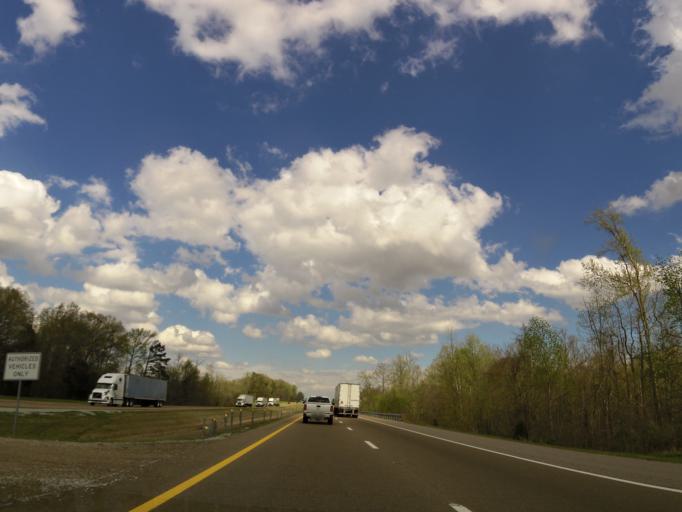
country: US
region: Tennessee
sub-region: Crockett County
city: Bells
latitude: 35.6280
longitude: -88.9658
